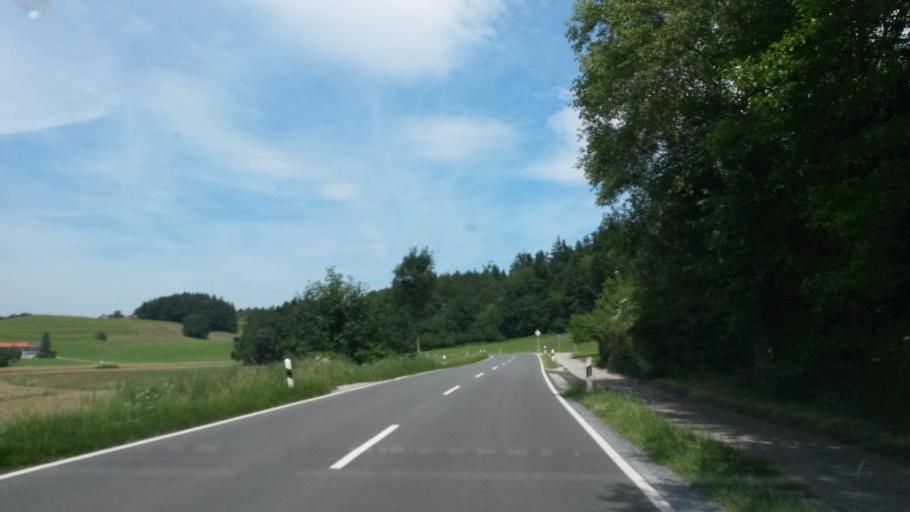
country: DE
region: Bavaria
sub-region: Upper Bavaria
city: Aschau im Chiemgau
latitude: 47.7917
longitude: 12.3419
